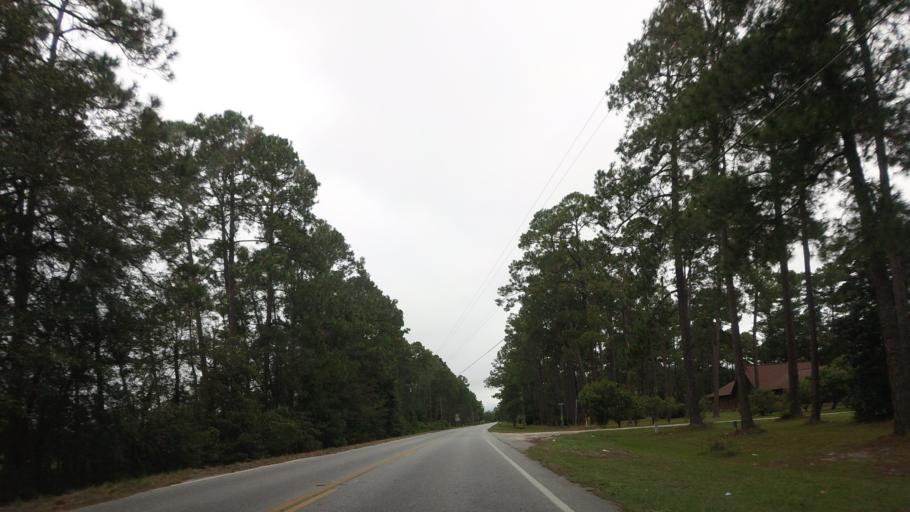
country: US
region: Georgia
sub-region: Berrien County
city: Ray City
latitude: 31.0569
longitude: -83.1978
